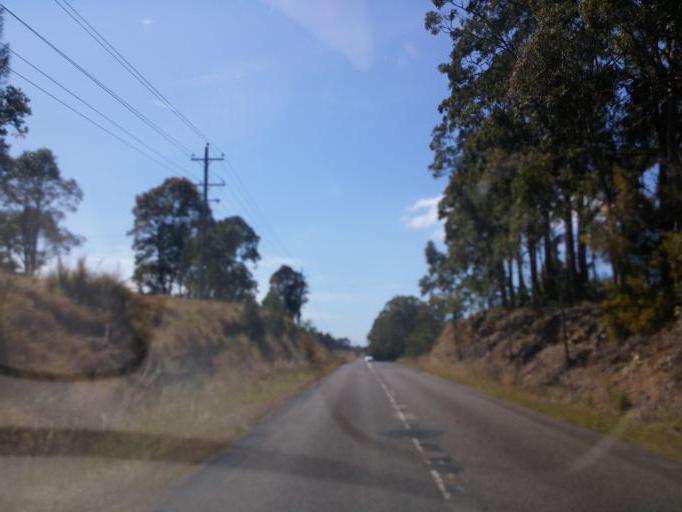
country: AU
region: New South Wales
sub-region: Great Lakes
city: Bulahdelah
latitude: -32.3777
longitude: 152.3751
